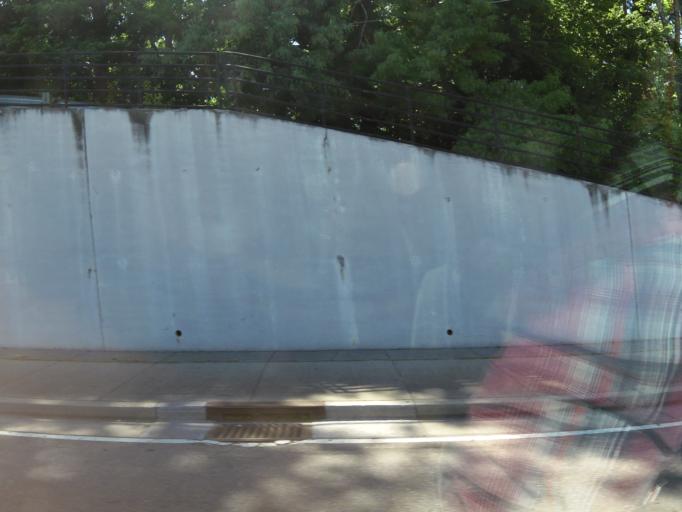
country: US
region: Tennessee
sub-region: Sevier County
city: Sevierville
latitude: 35.8532
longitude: -83.5698
